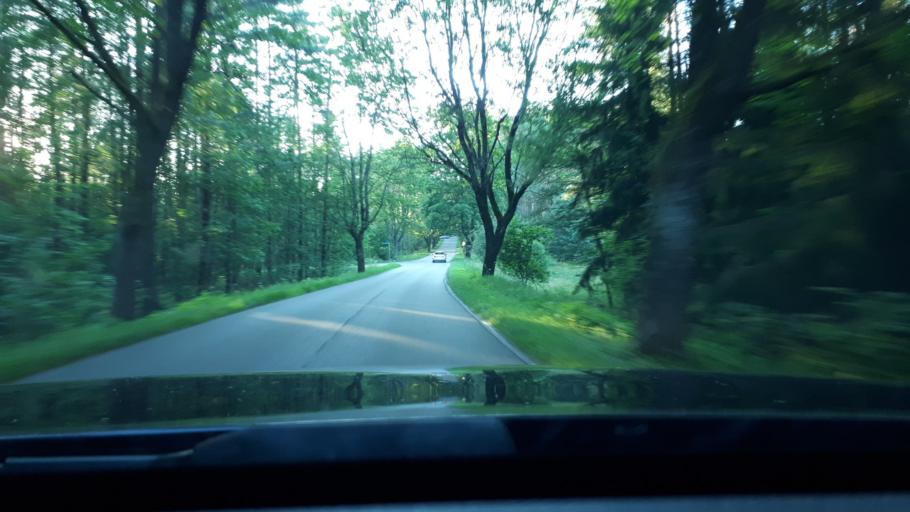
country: PL
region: Warmian-Masurian Voivodeship
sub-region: Powiat olsztynski
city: Stawiguda
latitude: 53.6108
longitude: 20.4193
